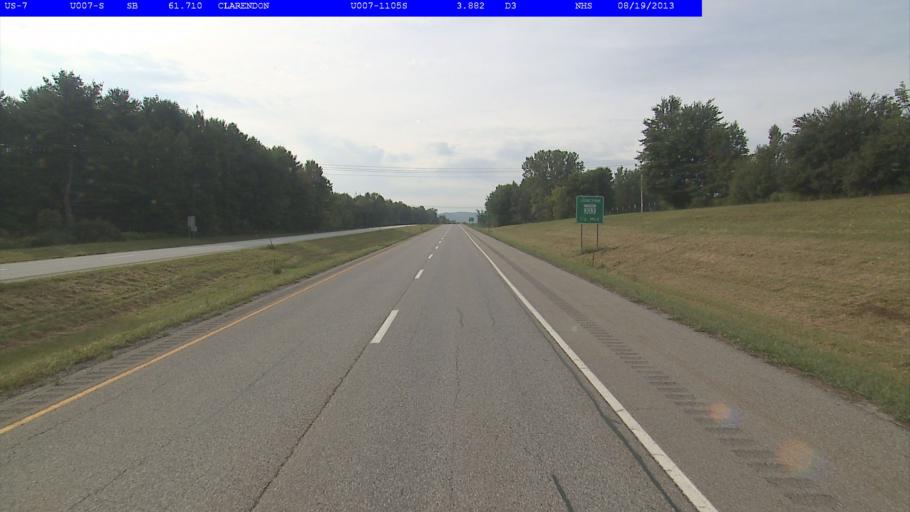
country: US
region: Vermont
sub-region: Rutland County
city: Rutland
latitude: 43.5483
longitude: -72.9617
